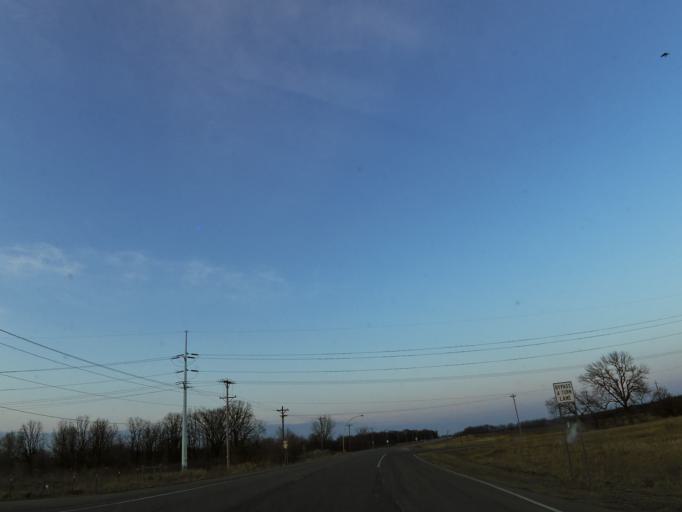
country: US
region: Minnesota
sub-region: Mower County
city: Austin
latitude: 43.6515
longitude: -92.9496
